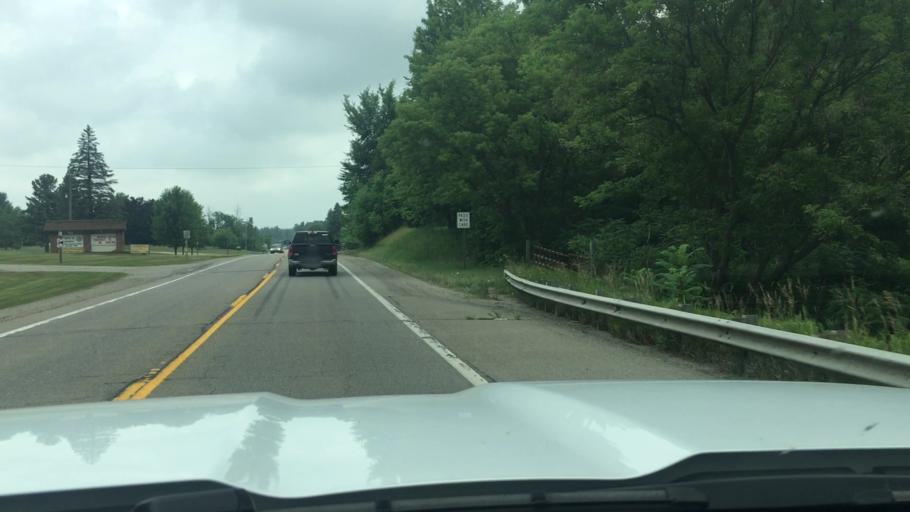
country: US
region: Michigan
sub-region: Lapeer County
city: Imlay City
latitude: 43.0767
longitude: -83.0754
